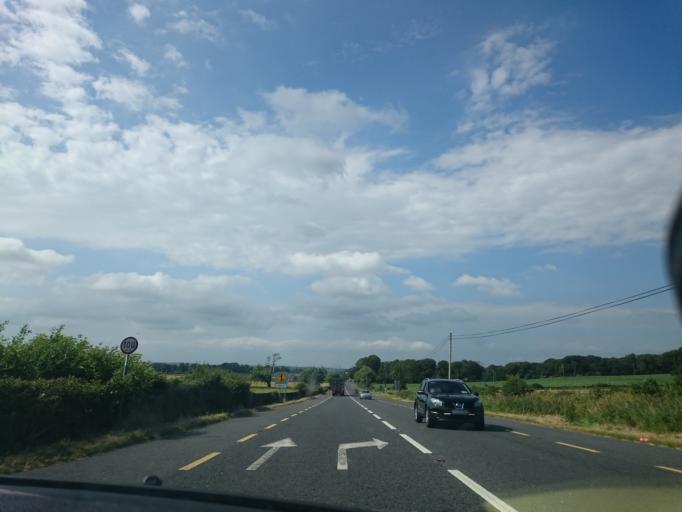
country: IE
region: Leinster
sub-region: Kilkenny
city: Kilkenny
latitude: 52.6168
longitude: -7.2474
